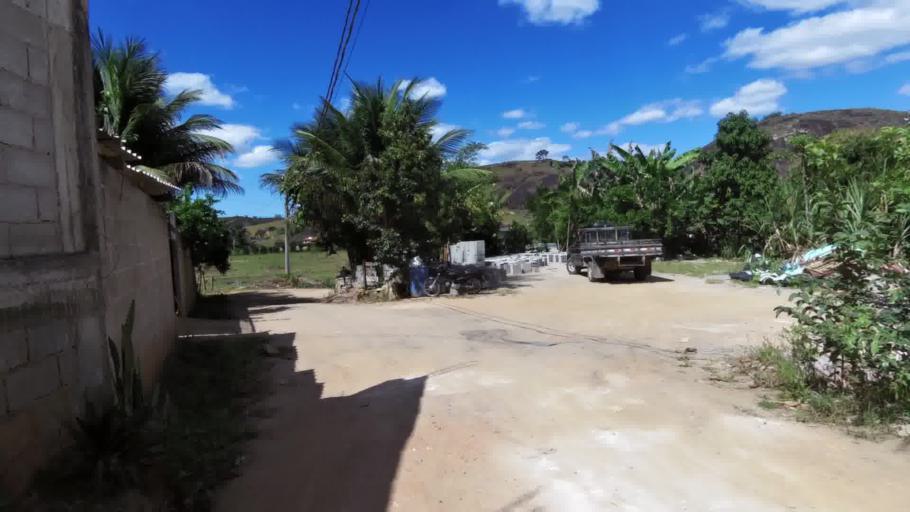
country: BR
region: Espirito Santo
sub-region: Rio Novo Do Sul
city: Rio Novo do Sul
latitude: -20.8604
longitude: -40.9487
